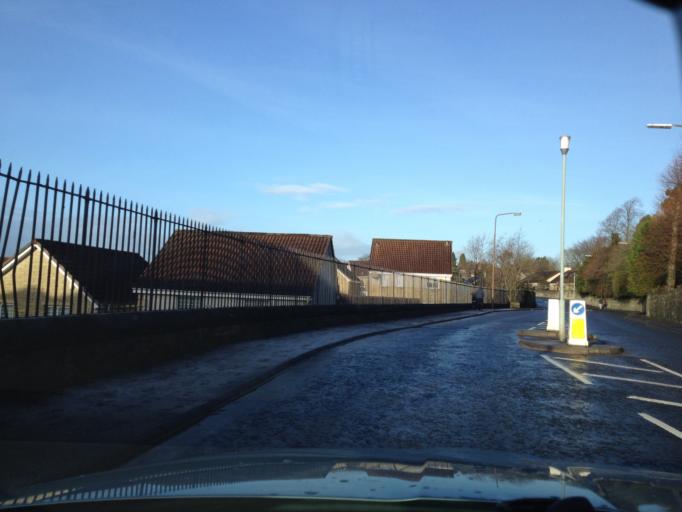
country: GB
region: Scotland
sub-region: West Lothian
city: Bathgate
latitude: 55.8957
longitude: -3.6262
